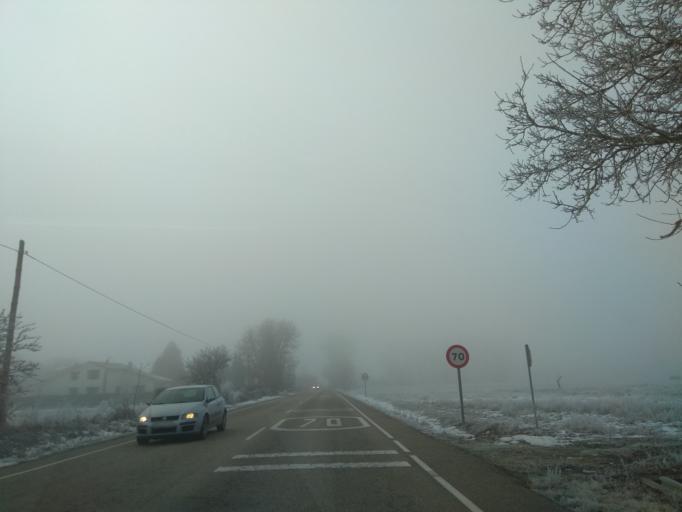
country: ES
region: Castille and Leon
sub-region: Provincia de Burgos
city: Espinosa de los Monteros
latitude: 43.0438
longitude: -3.4903
